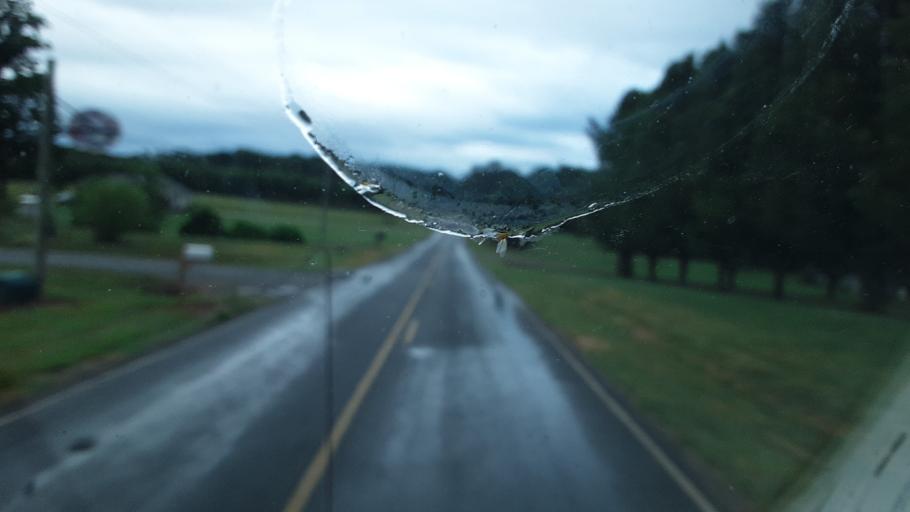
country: US
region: North Carolina
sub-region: Yadkin County
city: Jonesville
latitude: 36.0837
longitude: -80.8698
